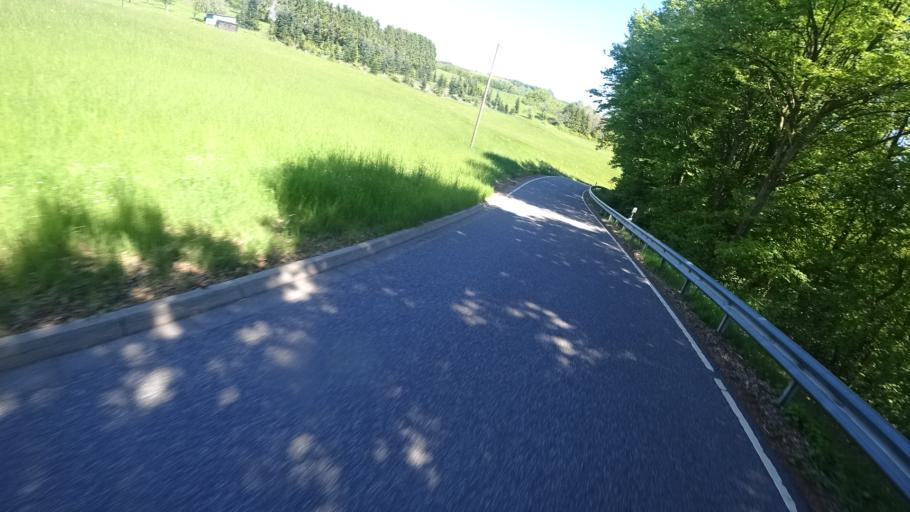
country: DE
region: Rheinland-Pfalz
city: Steineroth
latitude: 50.7471
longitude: 7.8555
